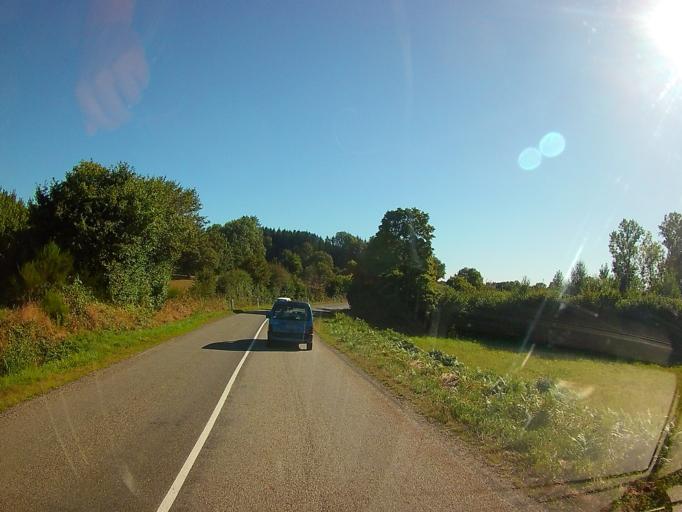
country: FR
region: Auvergne
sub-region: Departement du Puy-de-Dome
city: Saint-Ours
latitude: 45.8581
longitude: 2.8968
